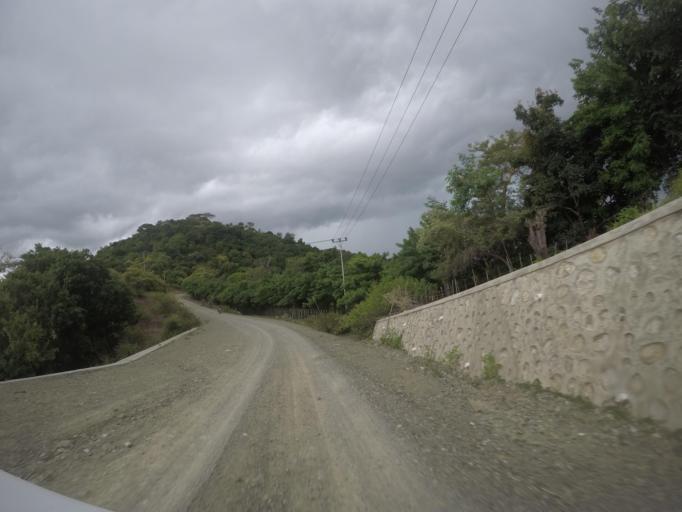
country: TL
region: Bobonaro
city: Maliana
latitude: -8.8491
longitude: 125.0633
